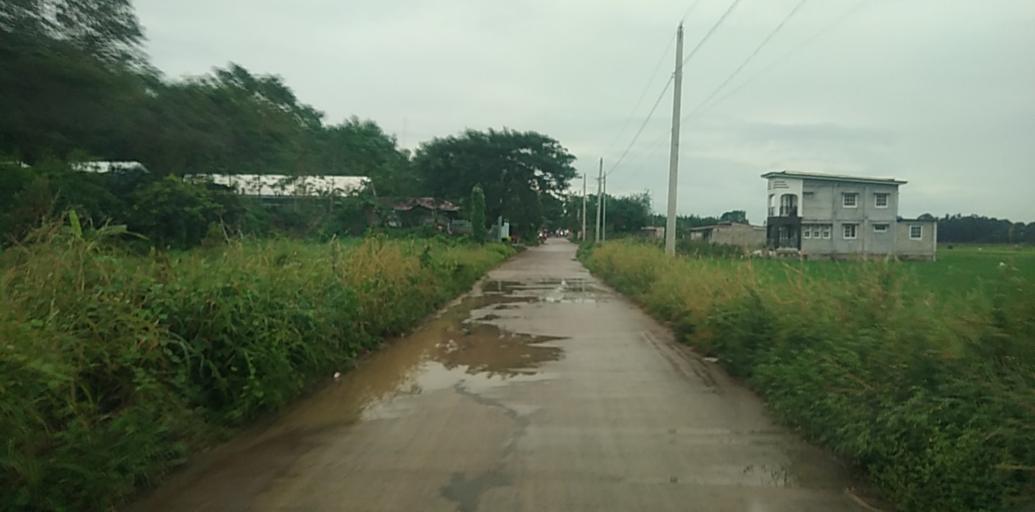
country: PH
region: Central Luzon
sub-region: Province of Pampanga
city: Arayat
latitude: 15.1599
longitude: 120.7404
